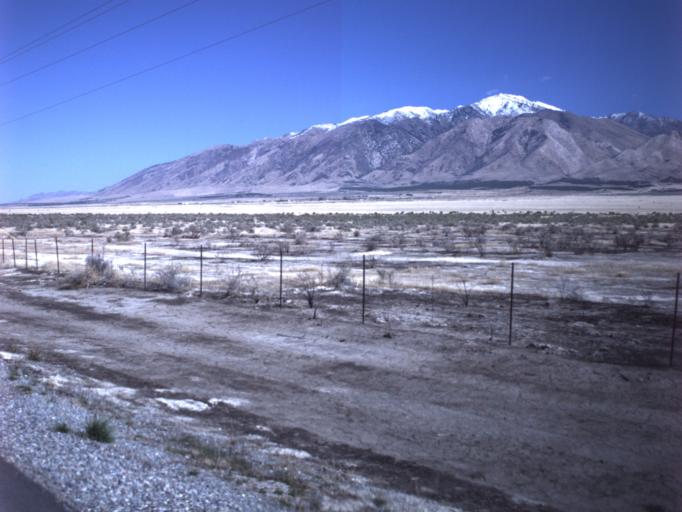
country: US
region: Utah
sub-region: Tooele County
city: Grantsville
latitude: 40.3677
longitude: -112.7462
